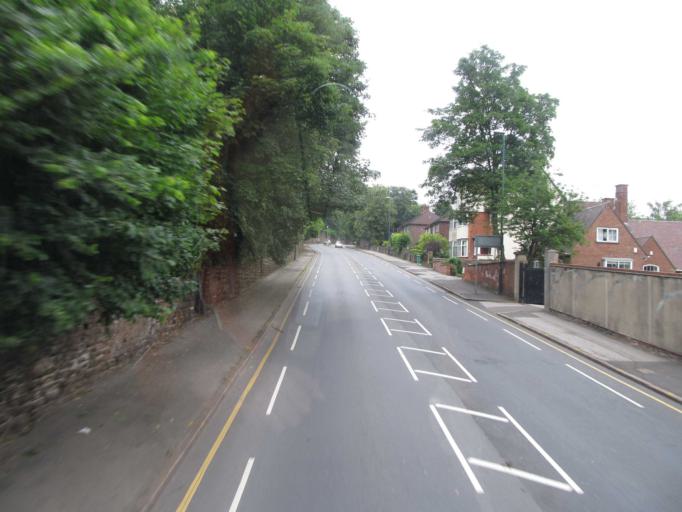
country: GB
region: England
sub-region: Nottingham
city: Nottingham
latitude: 52.9713
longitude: -1.1409
